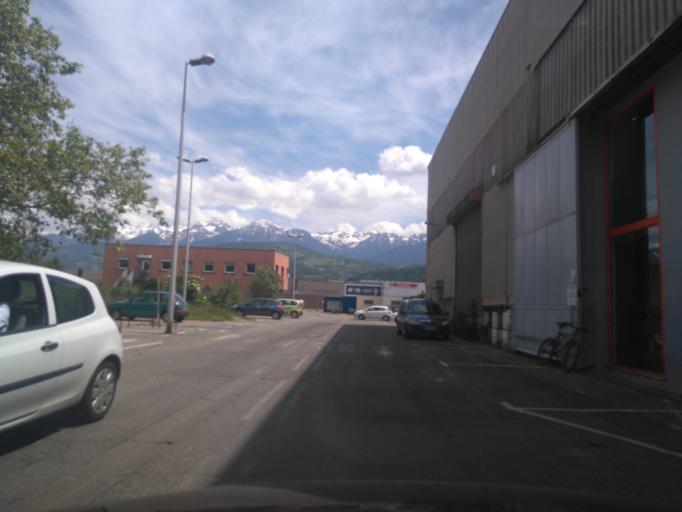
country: FR
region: Rhone-Alpes
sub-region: Departement de l'Isere
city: Saint-Martin-d'Heres
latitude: 45.1851
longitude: 5.7559
